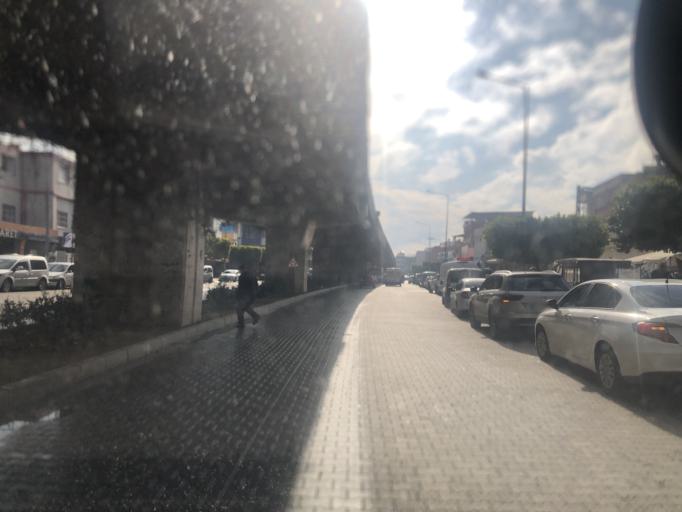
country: TR
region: Adana
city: Seyhan
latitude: 36.9836
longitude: 35.3200
